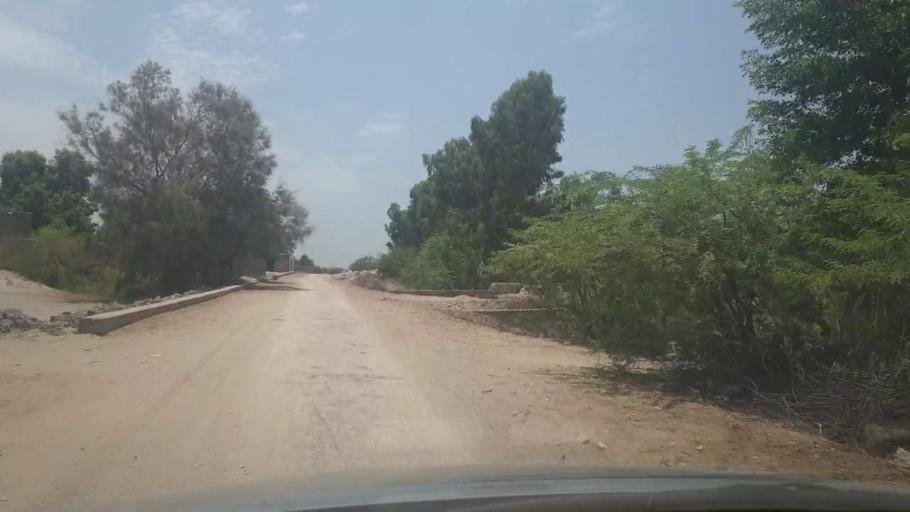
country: PK
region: Sindh
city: Kot Diji
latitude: 27.4110
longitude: 68.7351
